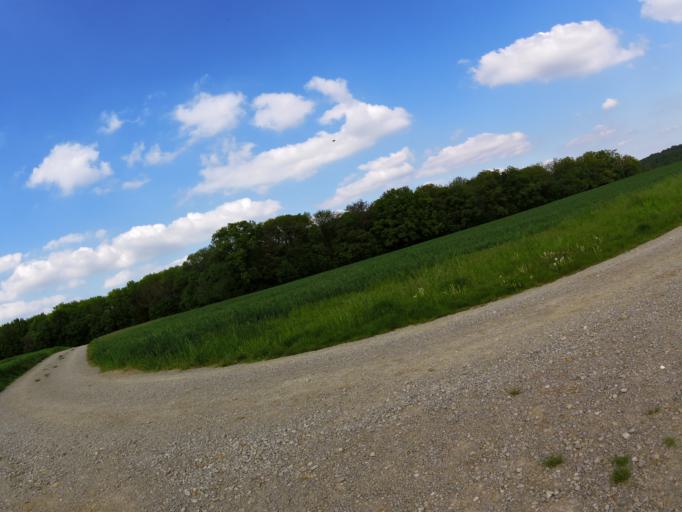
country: DE
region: Bavaria
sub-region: Regierungsbezirk Unterfranken
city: Reichenberg
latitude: 49.7377
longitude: 9.9076
